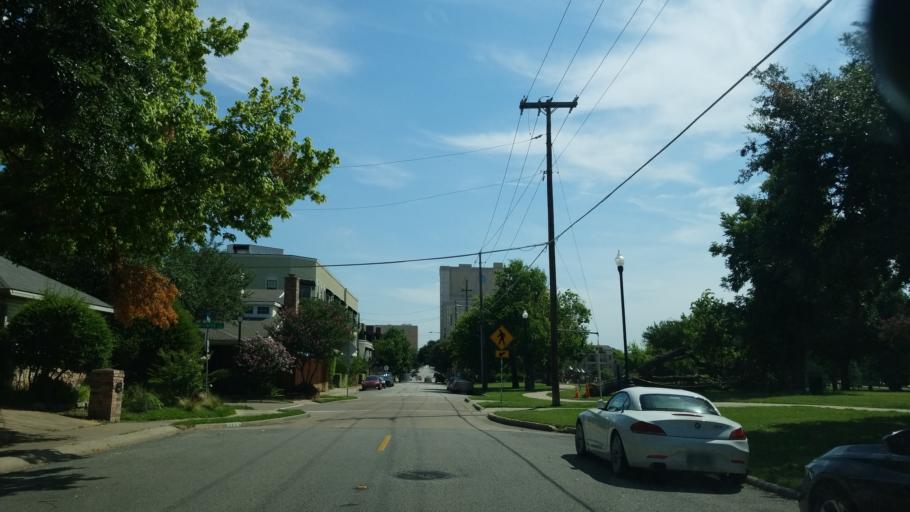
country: US
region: Texas
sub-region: Dallas County
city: Dallas
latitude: 32.7931
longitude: -96.7865
